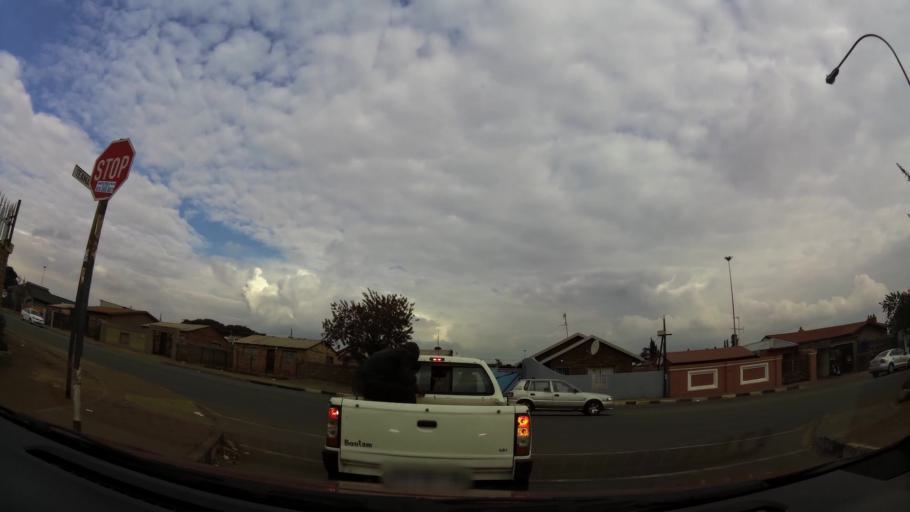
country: ZA
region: Gauteng
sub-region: City of Johannesburg Metropolitan Municipality
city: Soweto
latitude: -26.2485
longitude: 27.8418
